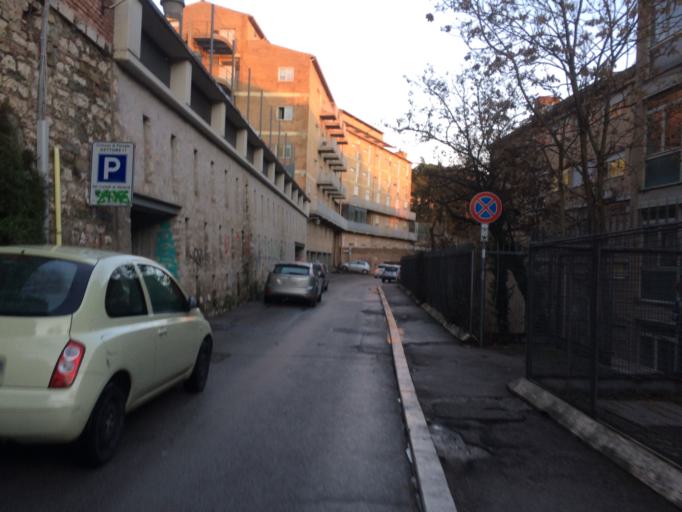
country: IT
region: Umbria
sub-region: Provincia di Perugia
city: Perugia
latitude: 43.1163
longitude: 12.3840
